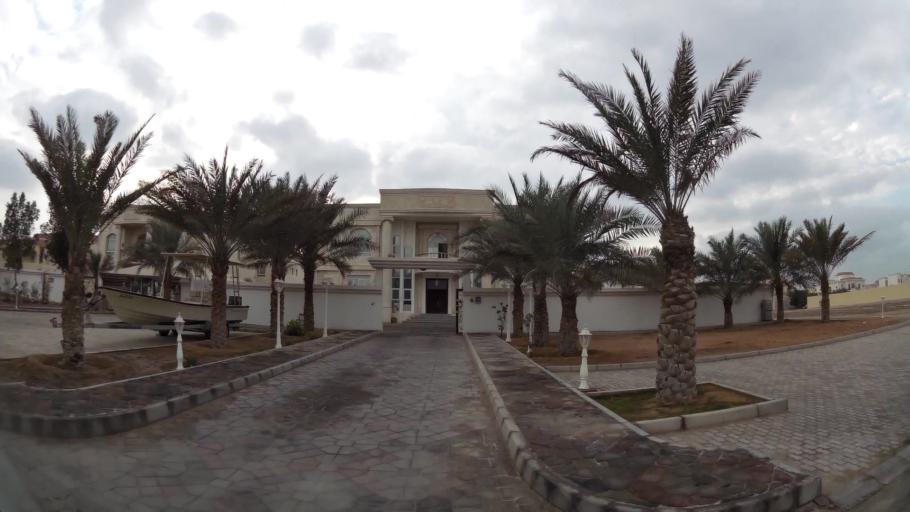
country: AE
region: Abu Dhabi
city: Abu Dhabi
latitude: 24.3600
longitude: 54.5455
